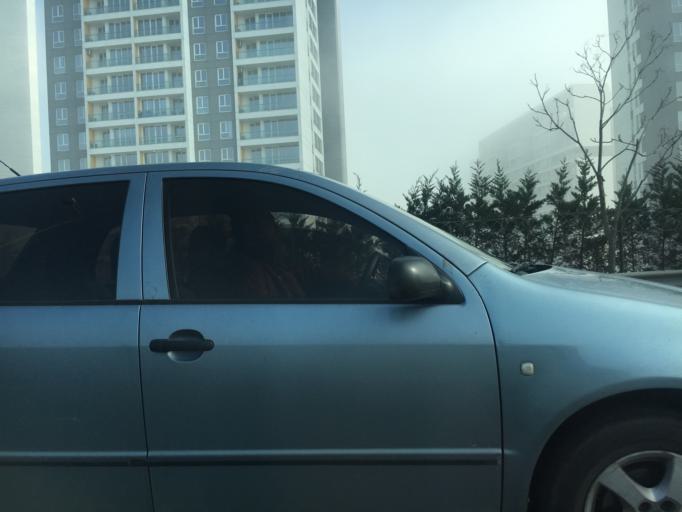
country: TR
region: Istanbul
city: Esenyurt
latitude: 41.0528
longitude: 28.6850
